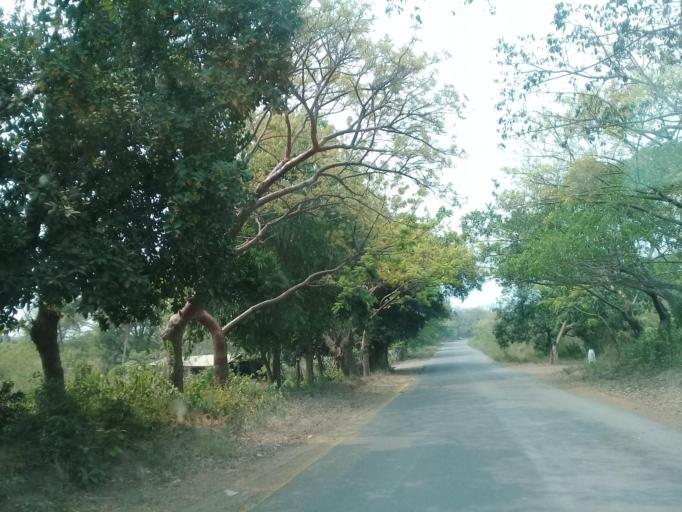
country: MX
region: Veracruz
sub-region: Medellin
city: La Laguna y Monte del Castillo
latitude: 18.9467
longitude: -96.1264
